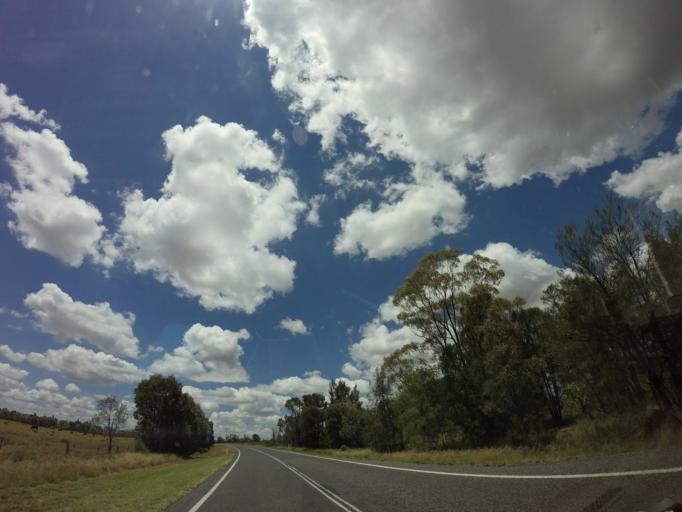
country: AU
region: Queensland
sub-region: Western Downs
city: Dalby
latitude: -27.9706
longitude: 151.1111
